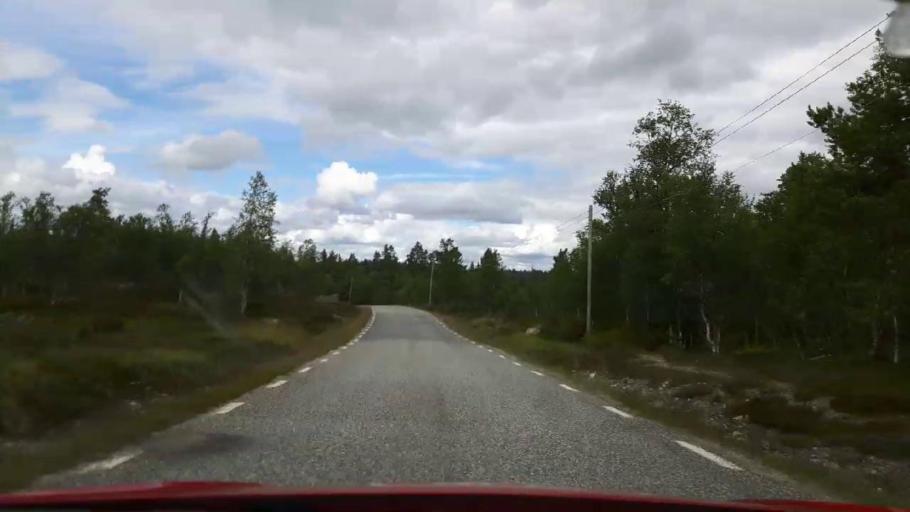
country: NO
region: Hedmark
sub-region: Engerdal
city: Engerdal
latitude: 62.3503
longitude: 12.7952
